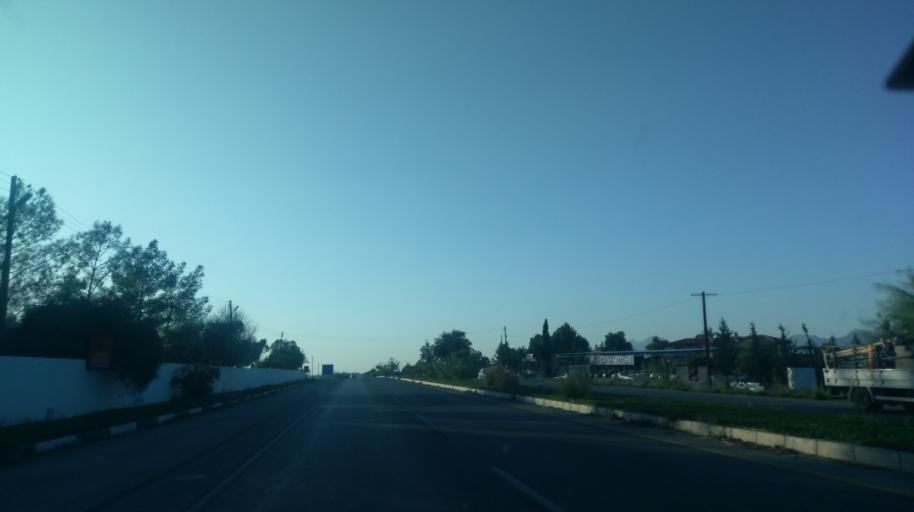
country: CY
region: Larnaka
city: Athienou
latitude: 35.2086
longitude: 33.5829
